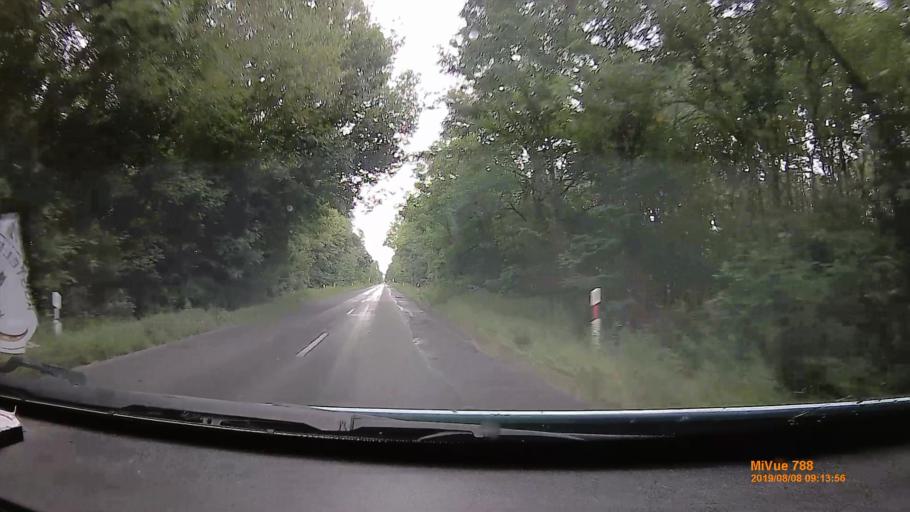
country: HU
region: Hajdu-Bihar
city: Hajdusamson
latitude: 47.5266
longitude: 21.7414
